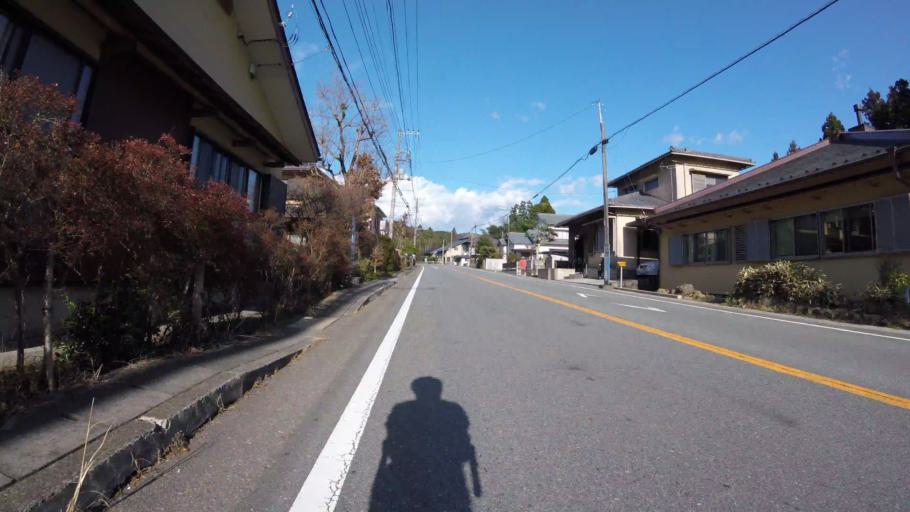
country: JP
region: Kanagawa
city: Hakone
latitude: 35.1557
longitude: 138.9954
